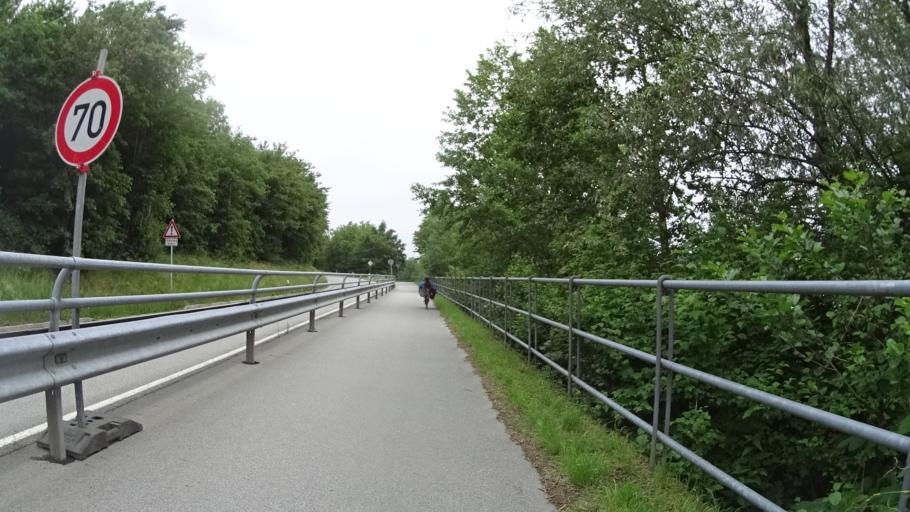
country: DE
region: Bavaria
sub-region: Lower Bavaria
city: Vilshofen
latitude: 48.6085
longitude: 13.2577
